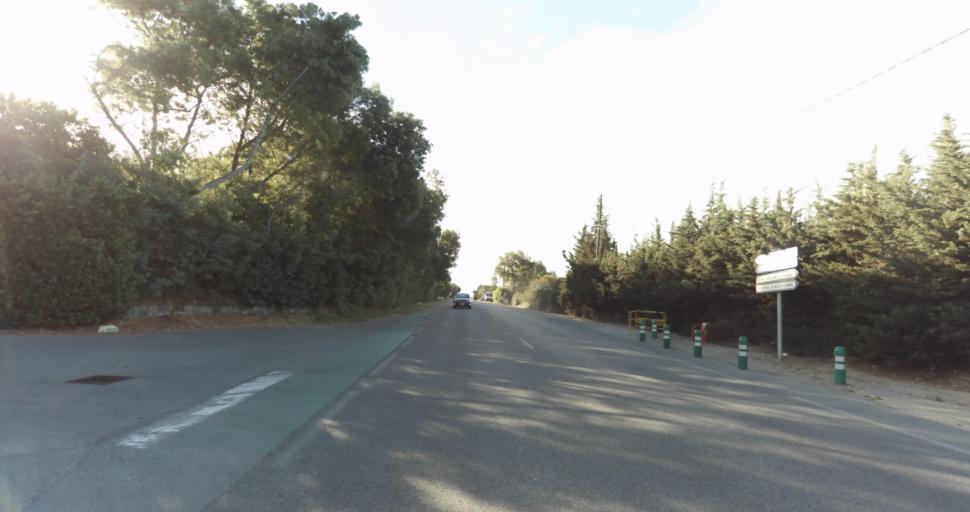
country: FR
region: Provence-Alpes-Cote d'Azur
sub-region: Departement du Var
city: Saint-Tropez
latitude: 43.2544
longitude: 6.6385
